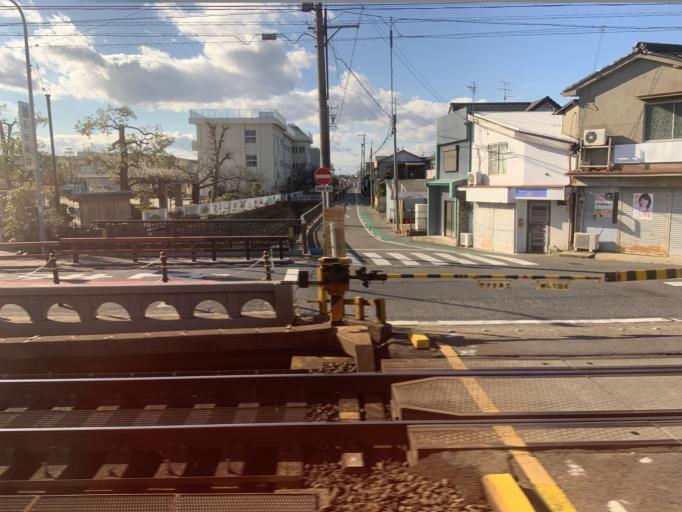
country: JP
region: Aichi
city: Kuroda
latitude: 35.3458
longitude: 136.7814
